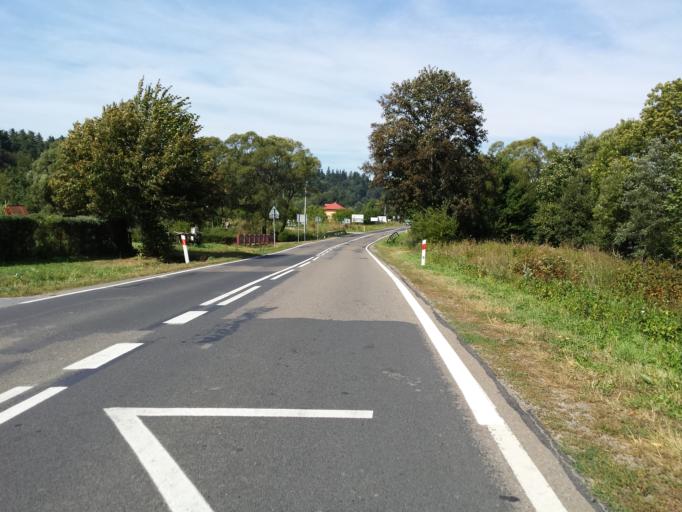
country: PL
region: Subcarpathian Voivodeship
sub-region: Powiat leski
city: Lesko
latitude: 49.4623
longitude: 22.3299
